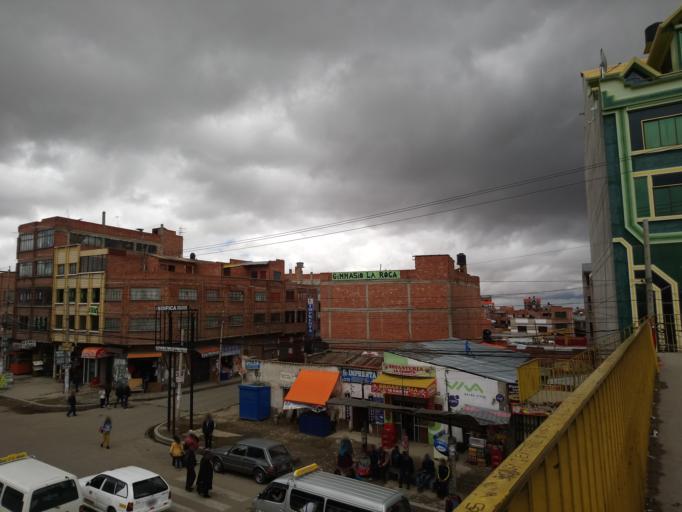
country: BO
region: La Paz
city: La Paz
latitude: -16.4840
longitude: -68.2053
